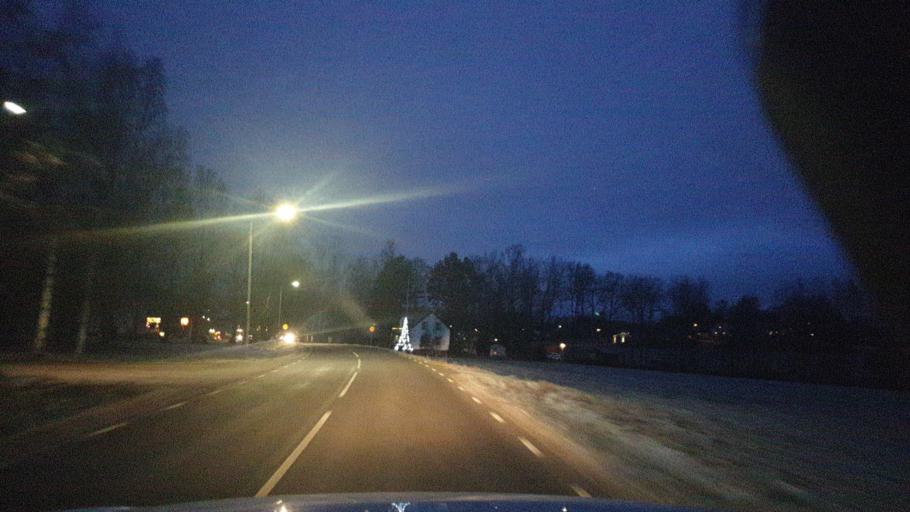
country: SE
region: Vaermland
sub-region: Arvika Kommun
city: Arvika
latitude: 59.5474
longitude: 12.5682
